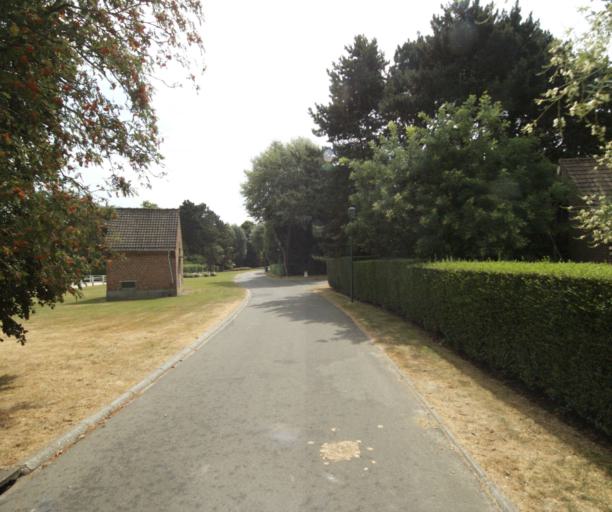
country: FR
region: Nord-Pas-de-Calais
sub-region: Departement du Nord
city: Bondues
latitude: 50.7205
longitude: 3.1149
